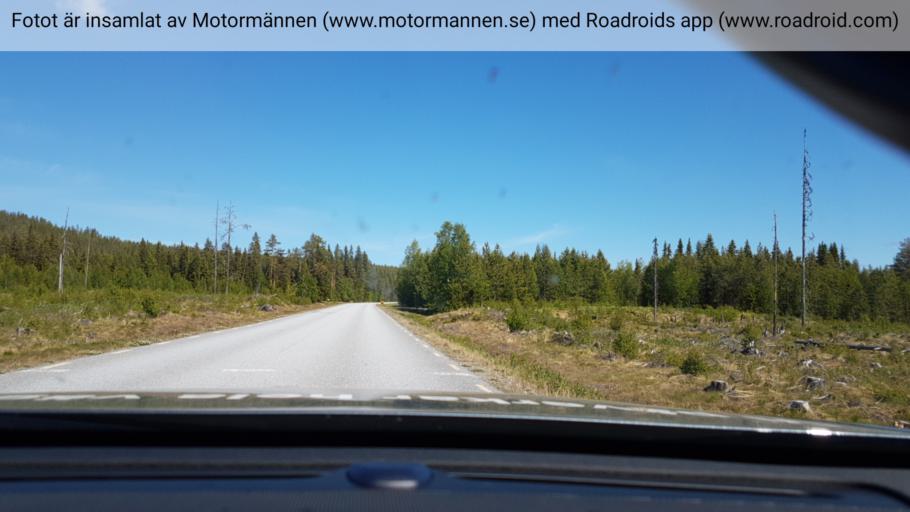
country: SE
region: Vaesterbotten
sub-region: Vilhelmina Kommun
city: Vilhelmina
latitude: 64.6320
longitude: 16.9026
